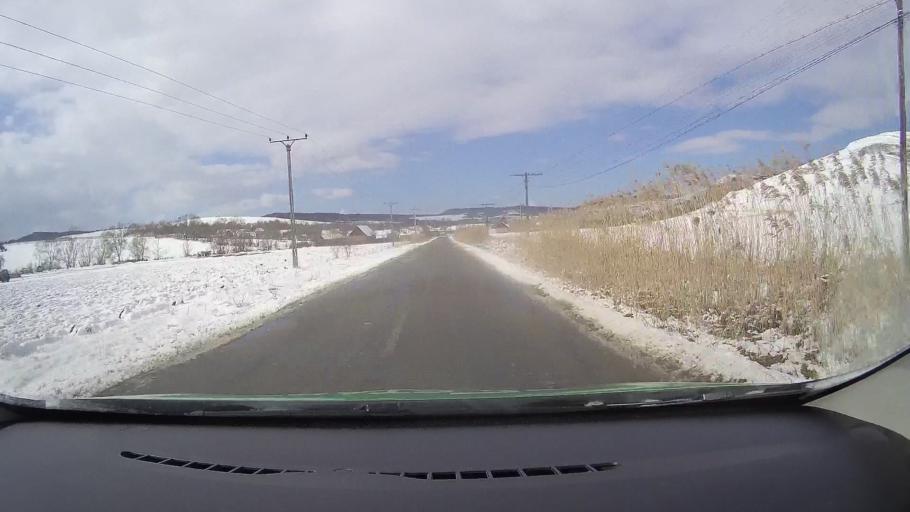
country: RO
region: Sibiu
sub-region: Comuna Altina
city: Altina
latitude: 45.9802
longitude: 24.4610
